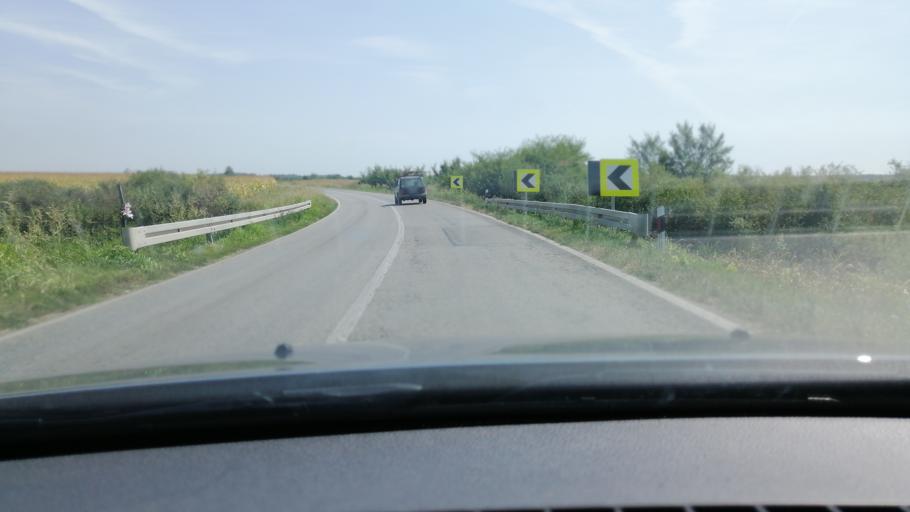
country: RS
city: Sutjeska
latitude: 45.3773
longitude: 20.7318
